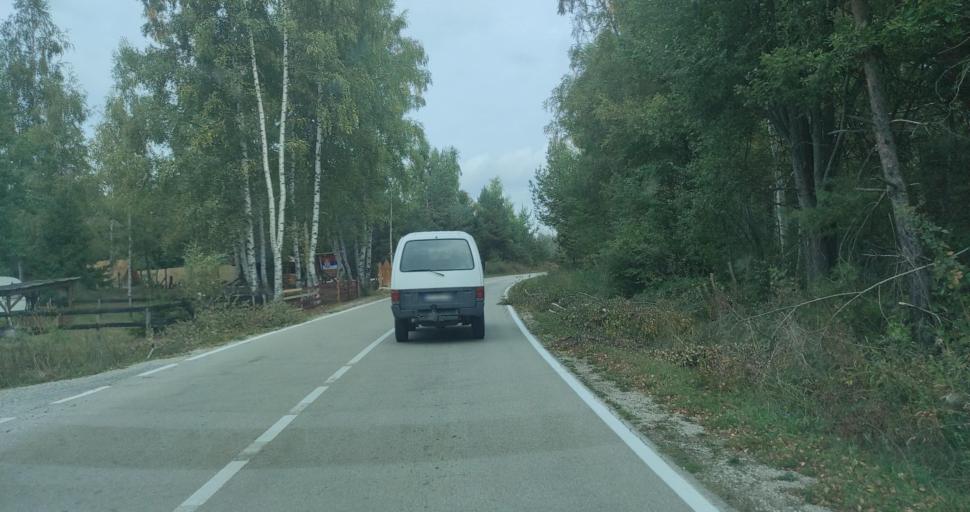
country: RS
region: Central Serbia
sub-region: Jablanicki Okrug
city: Crna Trava
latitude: 42.6779
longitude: 22.3120
